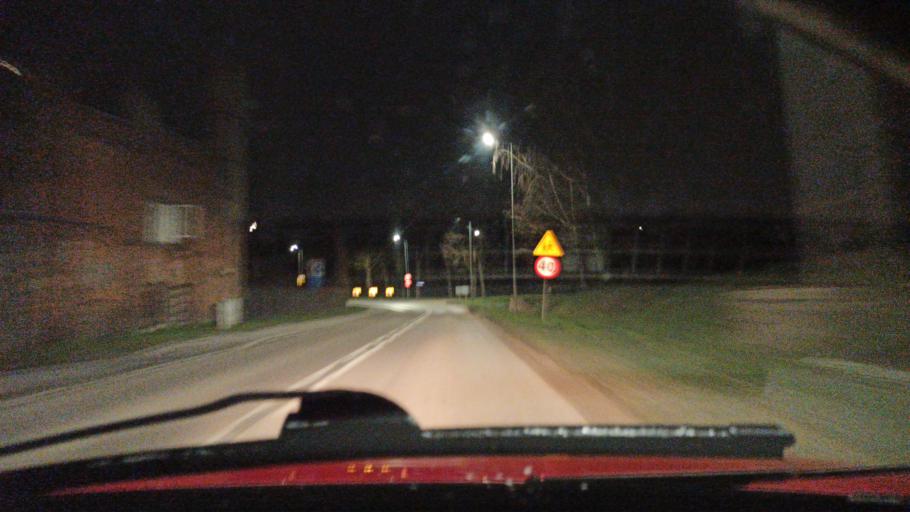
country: PL
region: Warmian-Masurian Voivodeship
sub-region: Powiat elblaski
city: Gronowo Gorne
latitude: 54.1576
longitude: 19.4385
